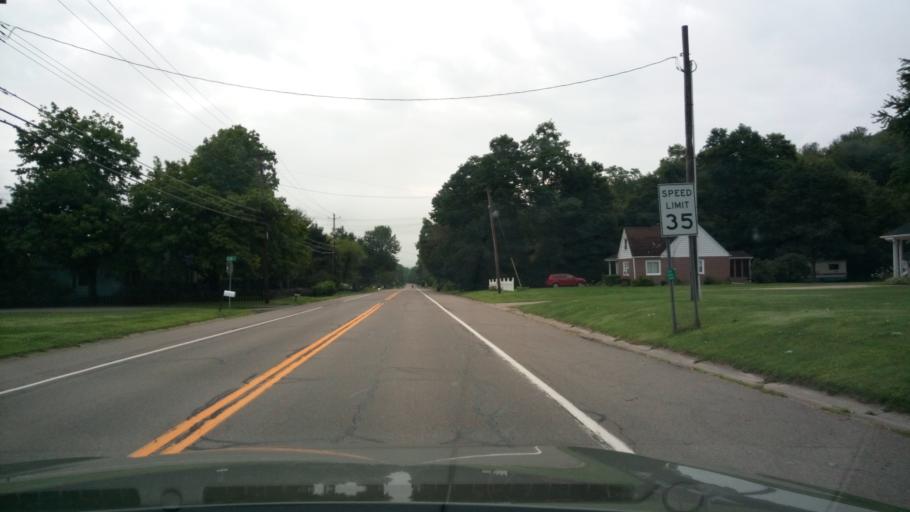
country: US
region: New York
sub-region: Chemung County
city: West Elmira
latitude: 42.0817
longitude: -76.8796
